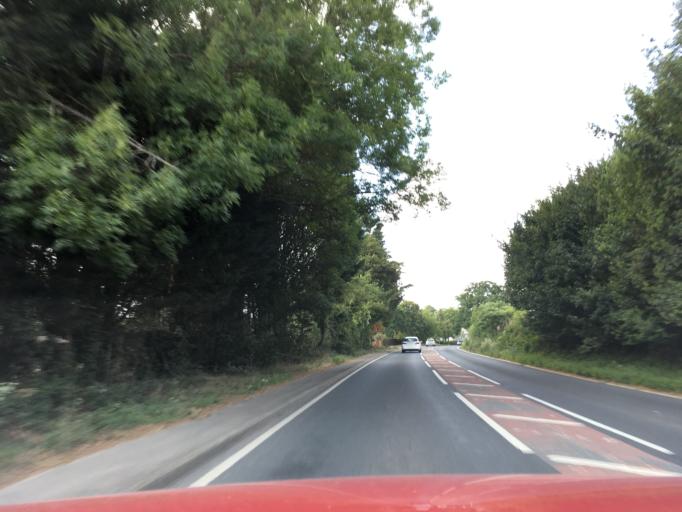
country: GB
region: England
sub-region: Kent
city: Headcorn
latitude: 51.2064
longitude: 0.5906
